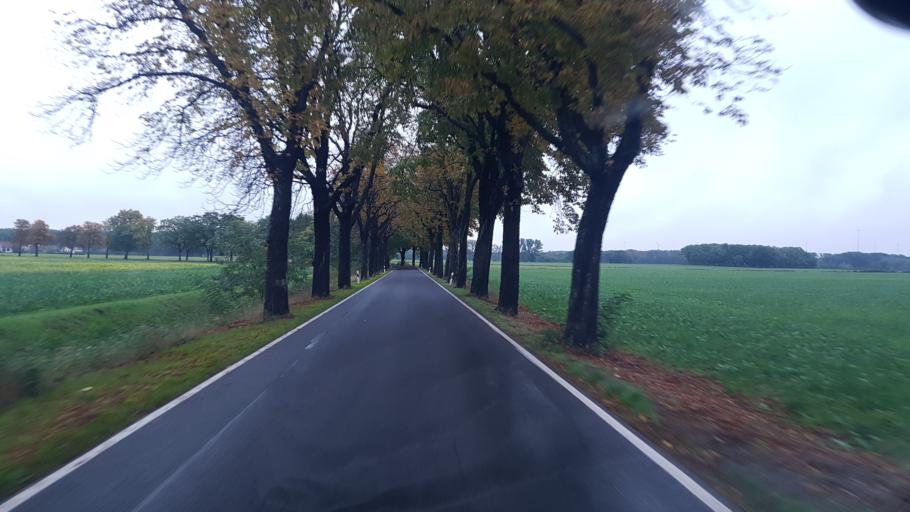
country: DE
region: Brandenburg
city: Bronkow
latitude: 51.6231
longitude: 13.9263
